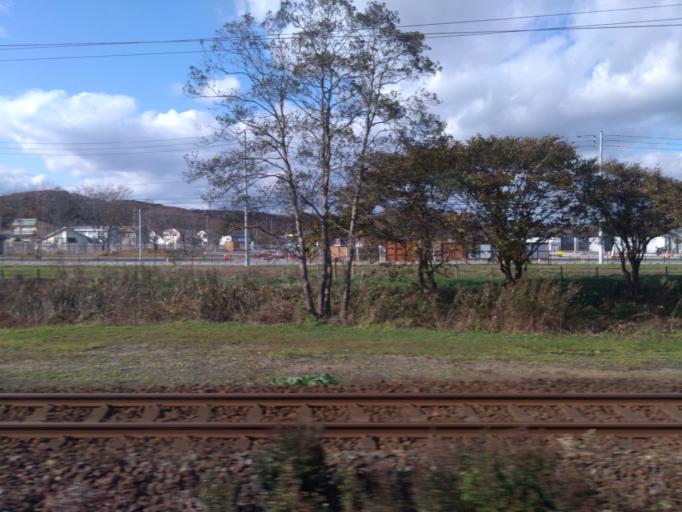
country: JP
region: Hokkaido
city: Shiraoi
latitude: 42.5574
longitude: 141.3641
